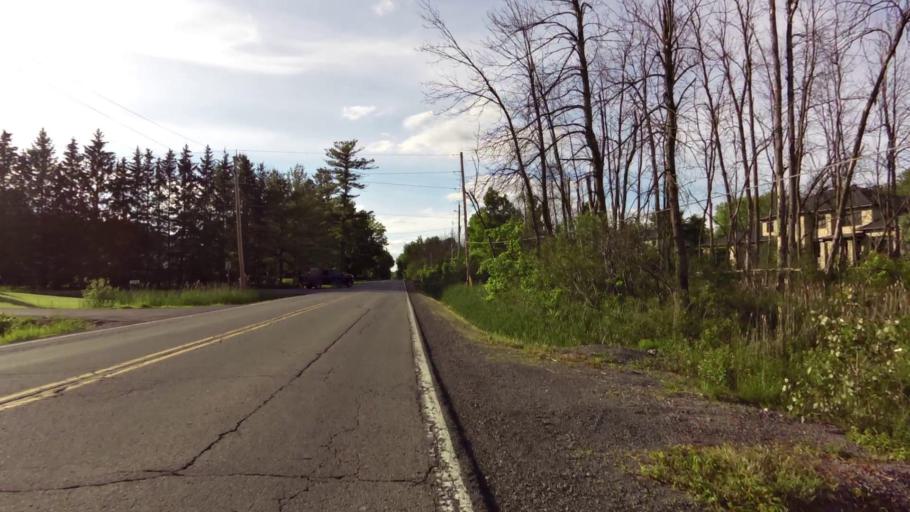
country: CA
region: Ontario
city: Ottawa
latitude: 45.2381
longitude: -75.6133
